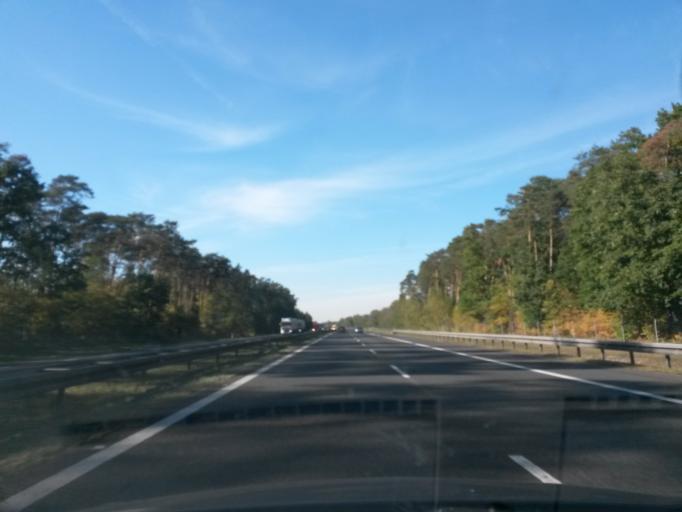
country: PL
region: Opole Voivodeship
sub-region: Powiat brzeski
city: Lewin Brzeski
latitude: 50.6979
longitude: 17.6221
